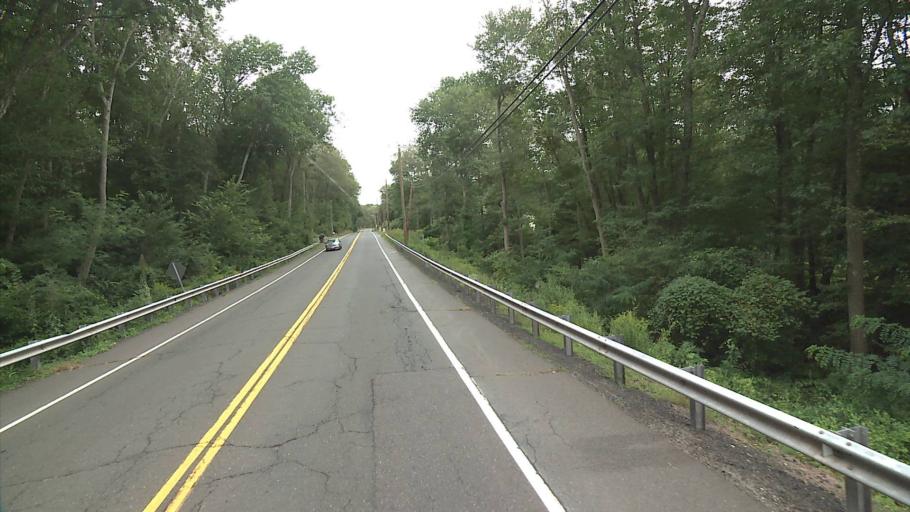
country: US
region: Connecticut
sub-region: Hartford County
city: Manchester
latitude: 41.7609
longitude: -72.4471
